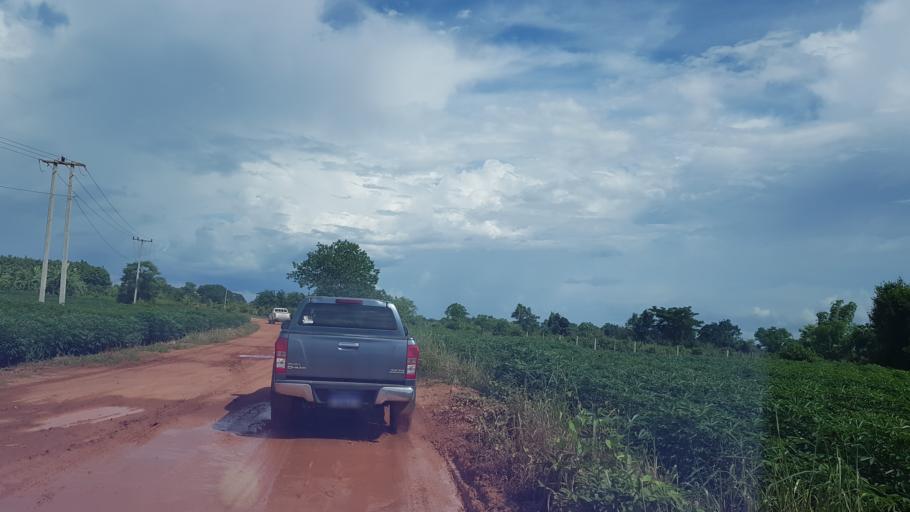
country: LA
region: Vientiane
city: Vientiane
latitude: 18.2267
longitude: 102.5647
